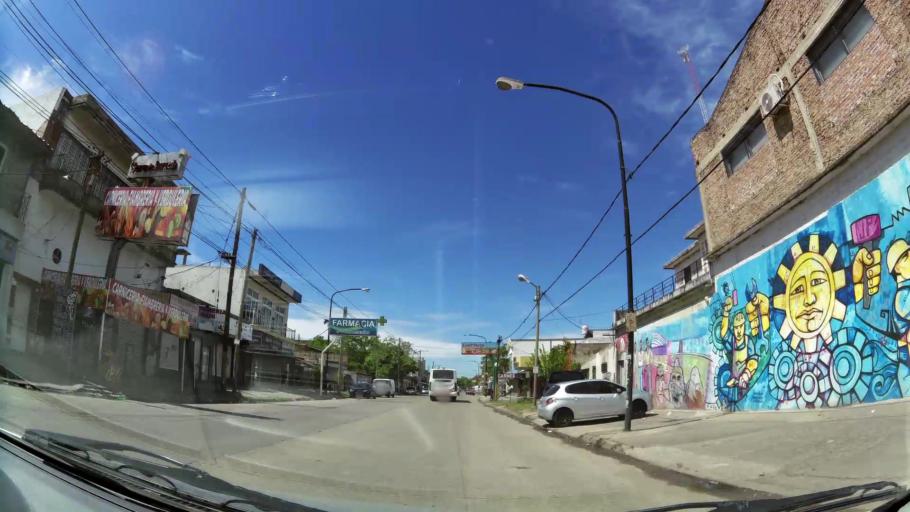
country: AR
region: Buenos Aires
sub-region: Partido de Quilmes
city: Quilmes
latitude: -34.7467
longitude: -58.2981
